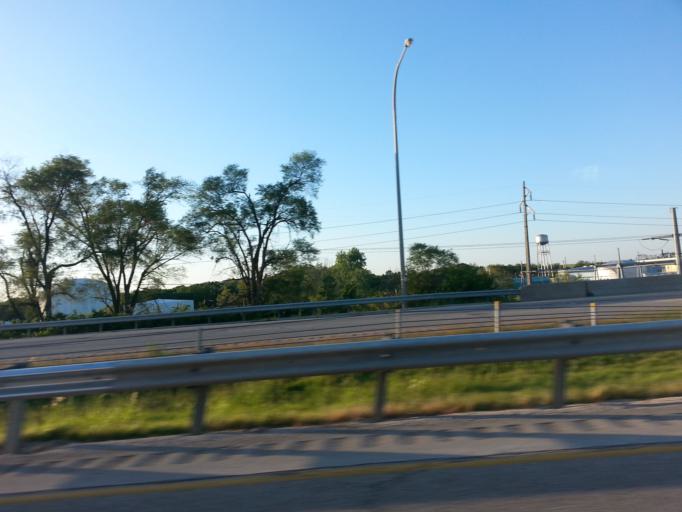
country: US
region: Illinois
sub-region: Vermilion County
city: Tilton
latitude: 40.1046
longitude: -87.6553
